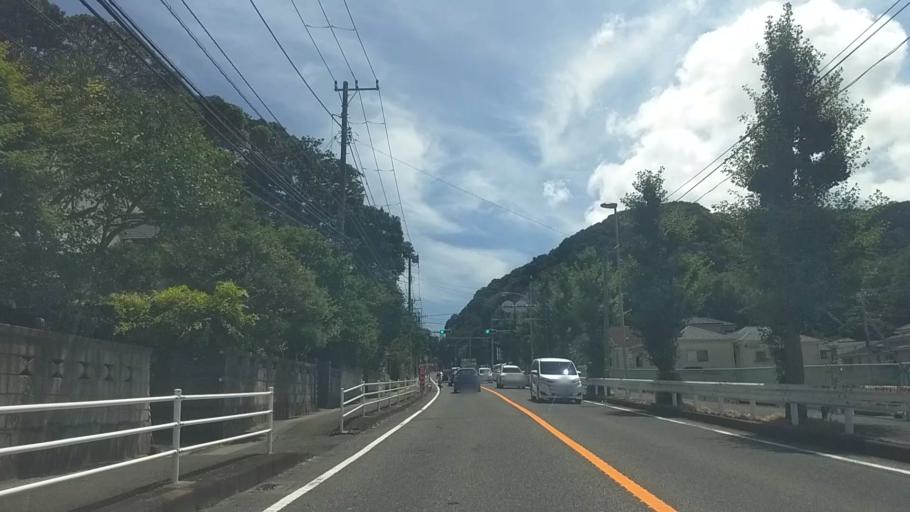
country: JP
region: Kanagawa
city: Yokosuka
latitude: 35.2505
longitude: 139.6652
